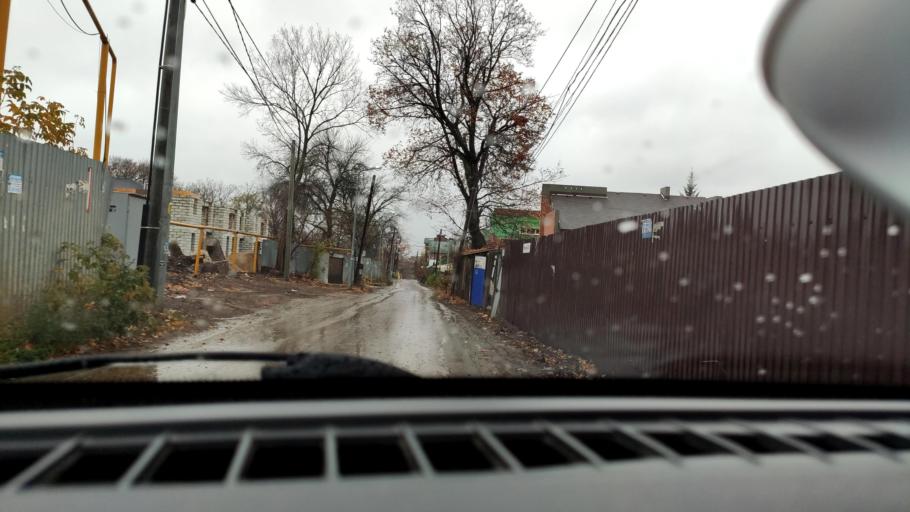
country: RU
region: Samara
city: Samara
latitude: 53.2338
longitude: 50.1739
